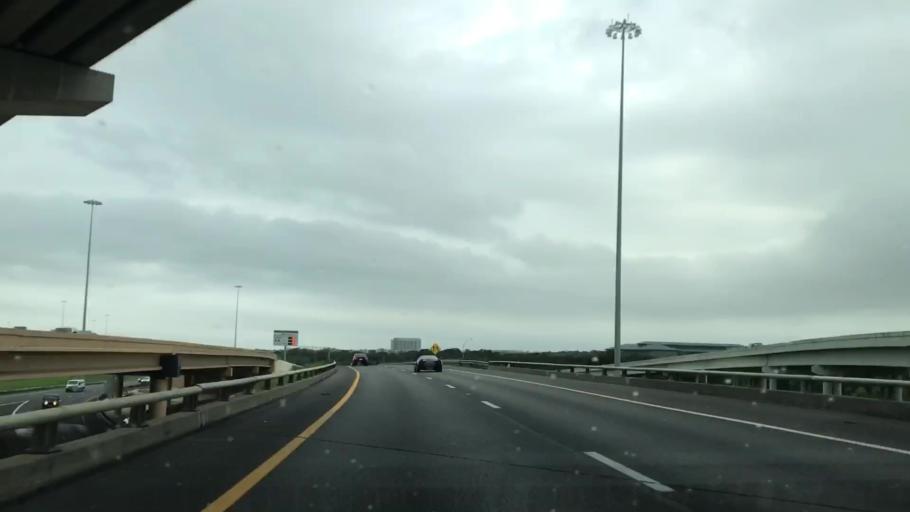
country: US
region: Texas
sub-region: Dallas County
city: Irving
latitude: 32.8809
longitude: -96.9478
